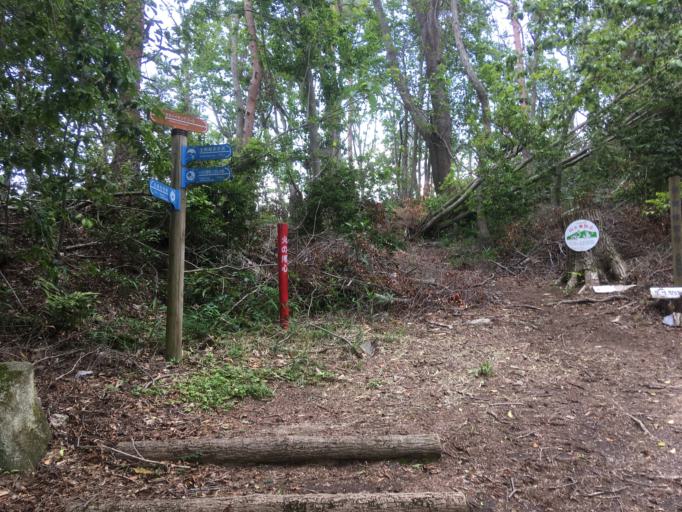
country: JP
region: Nara
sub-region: Ikoma-shi
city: Ikoma
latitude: 34.6922
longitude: 135.6666
